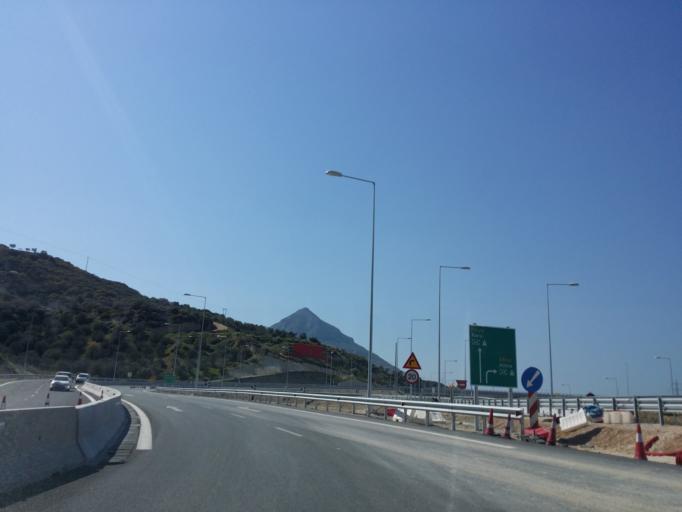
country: GR
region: Peloponnese
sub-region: Nomos Korinthias
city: Xylokastro
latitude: 38.0727
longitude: 22.6157
